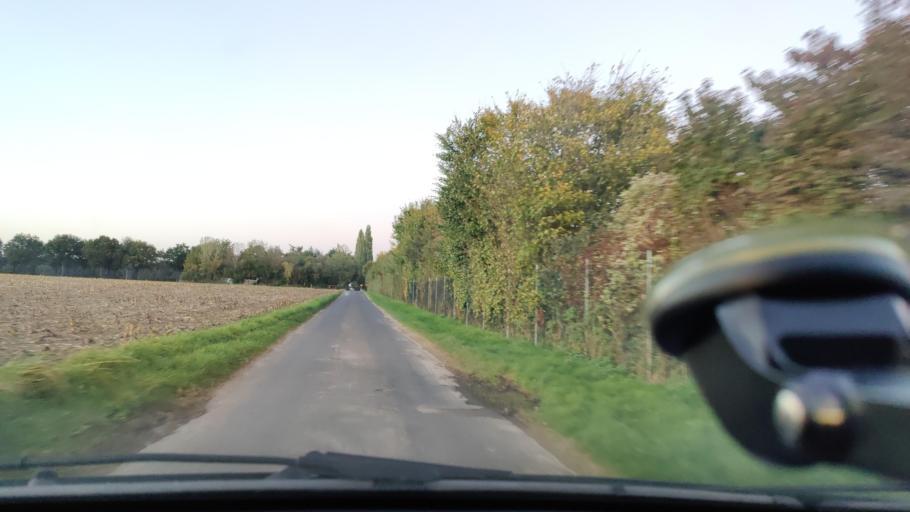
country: DE
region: North Rhine-Westphalia
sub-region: Regierungsbezirk Dusseldorf
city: Goch
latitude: 51.7166
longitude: 6.1805
